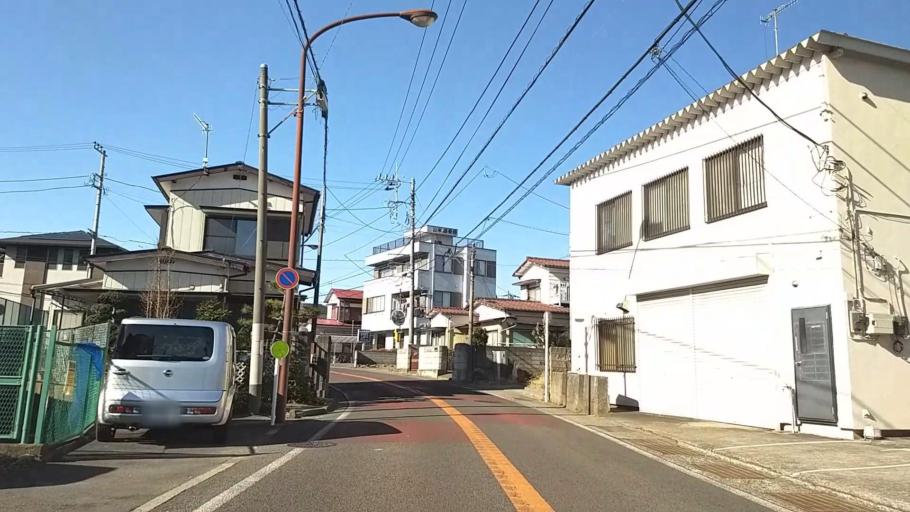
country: JP
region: Kanagawa
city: Hadano
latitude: 35.3731
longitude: 139.2190
